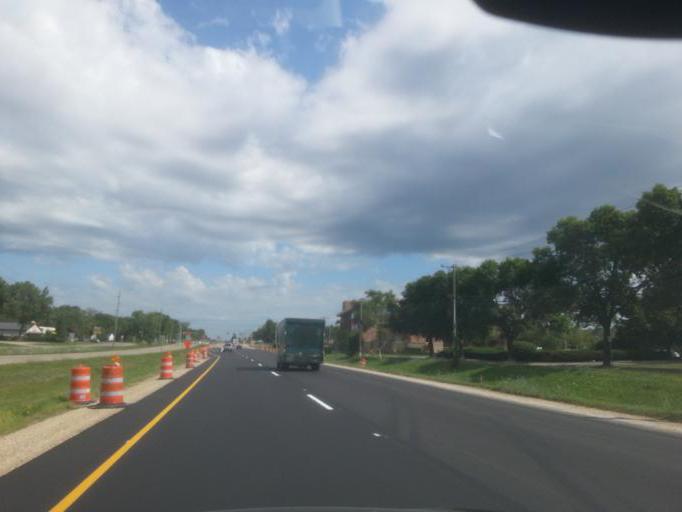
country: US
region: Wisconsin
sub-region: Dane County
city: Monona
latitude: 43.0703
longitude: -89.3093
